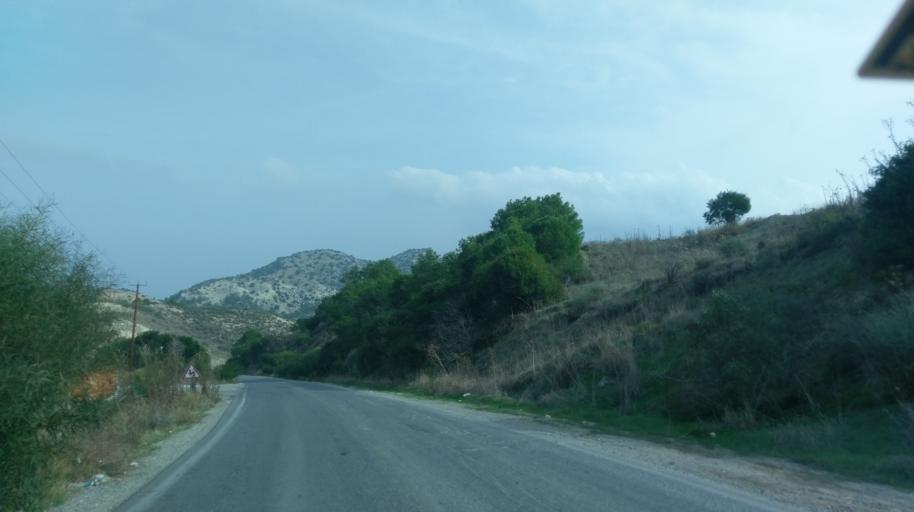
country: CY
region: Keryneia
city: Lapithos
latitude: 35.3284
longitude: 33.0636
